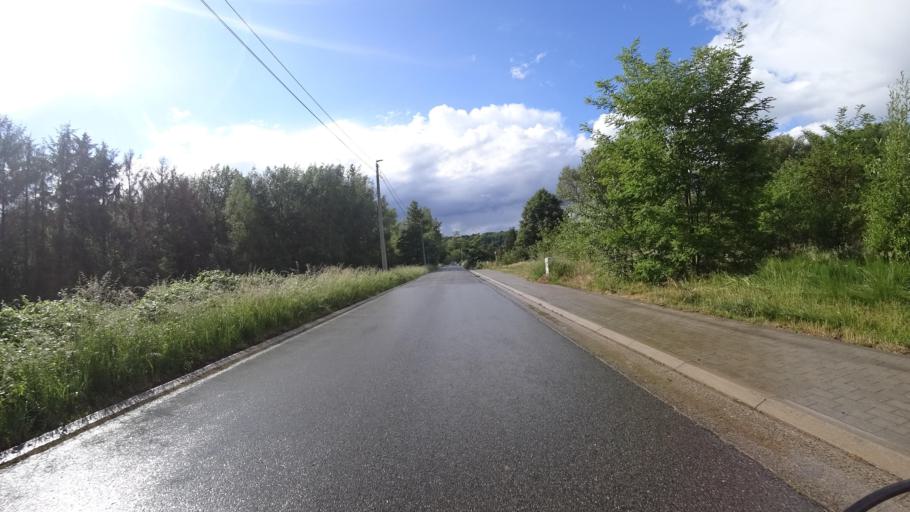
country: BE
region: Wallonia
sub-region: Province du Brabant Wallon
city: Wavre
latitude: 50.7038
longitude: 4.6019
